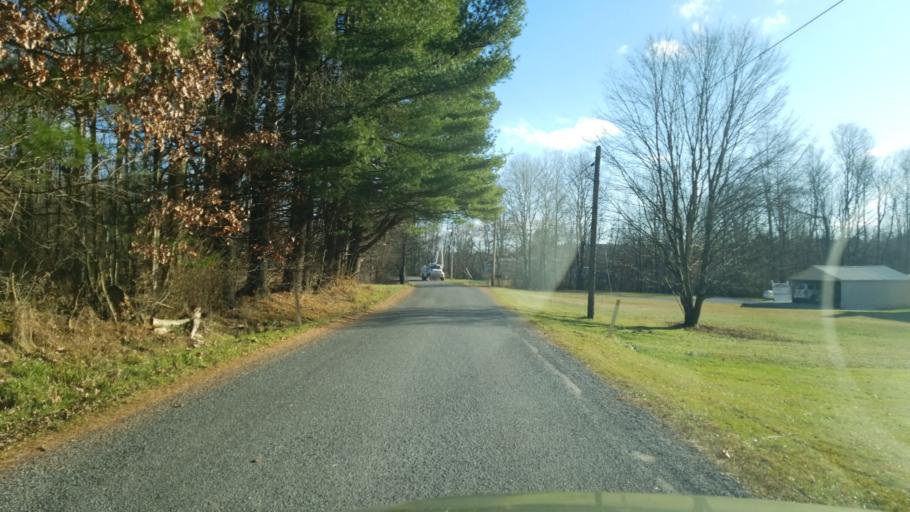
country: US
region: Pennsylvania
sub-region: Jefferson County
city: Brockway
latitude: 41.2628
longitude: -78.8038
